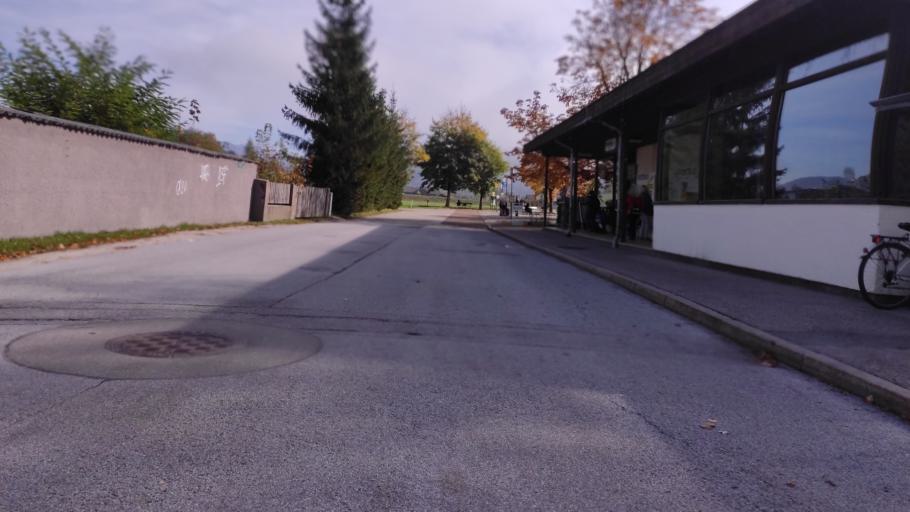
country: AT
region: Salzburg
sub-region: Politischer Bezirk Salzburg-Umgebung
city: Strobl
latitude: 47.7164
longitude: 13.4875
